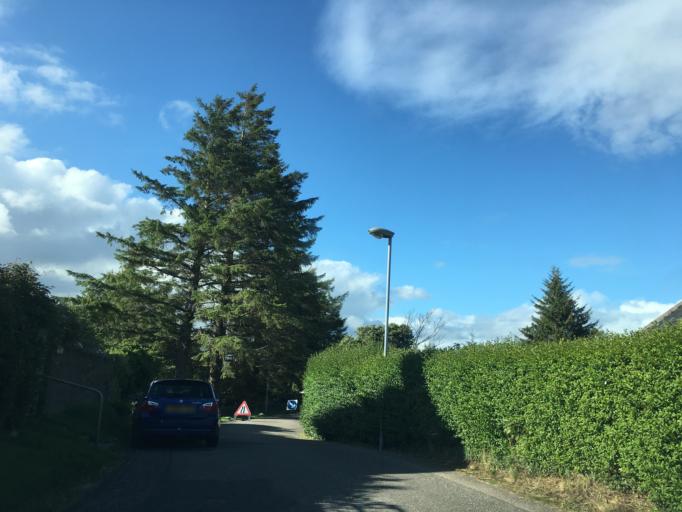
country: GB
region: Scotland
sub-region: Argyll and Bute
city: Oban
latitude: 56.4084
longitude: -5.4824
